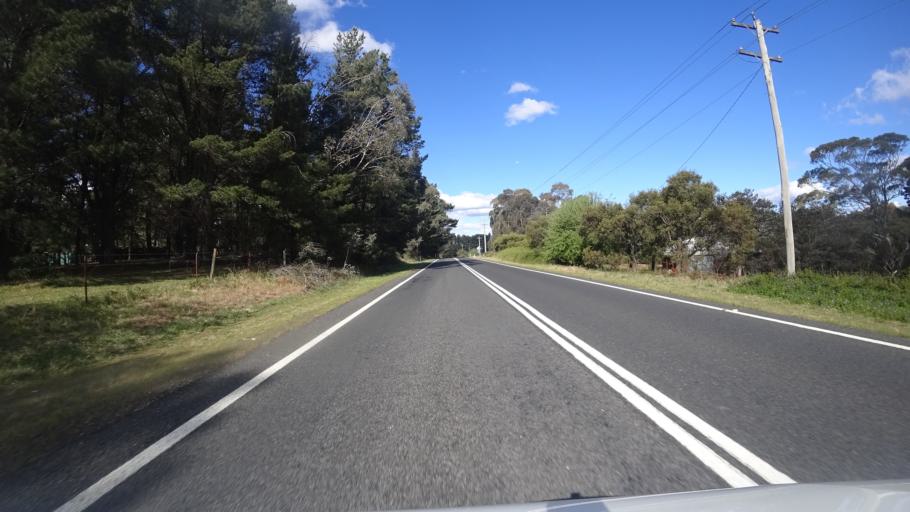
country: AU
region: New South Wales
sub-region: Lithgow
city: Bowenfels
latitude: -33.6370
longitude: 150.0738
